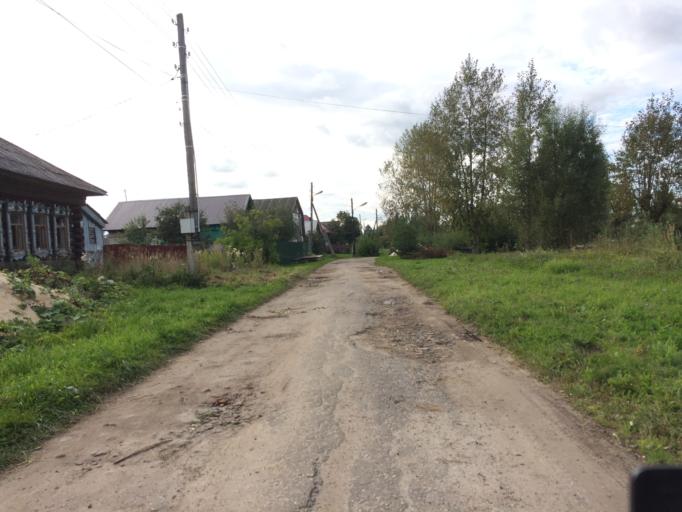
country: RU
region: Mariy-El
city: Yoshkar-Ola
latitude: 56.6523
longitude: 48.0156
